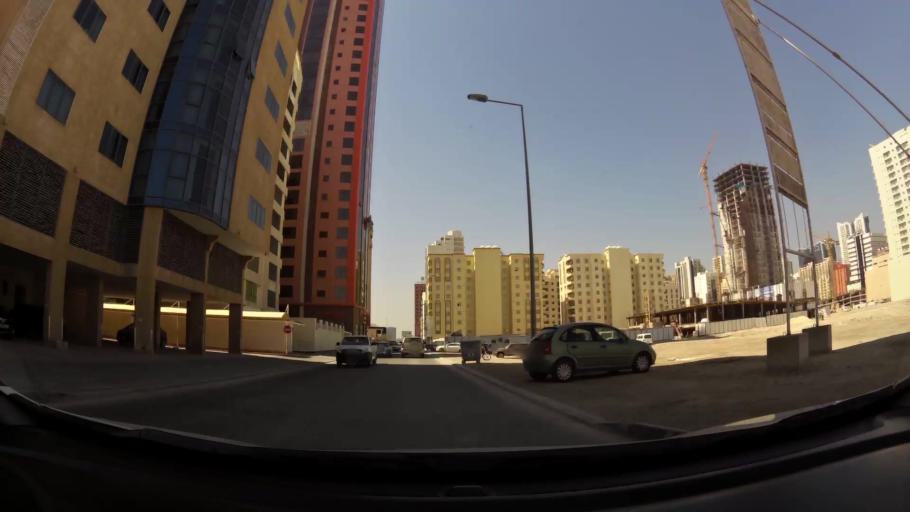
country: BH
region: Manama
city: Manama
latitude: 26.2169
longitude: 50.6122
